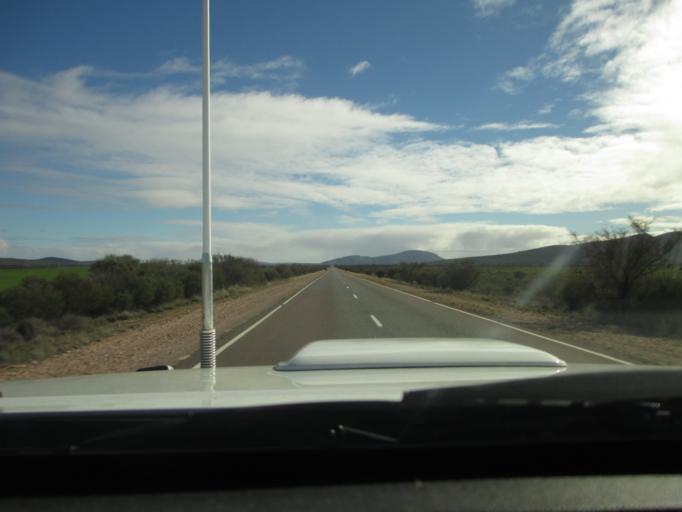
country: AU
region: South Australia
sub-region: Flinders Ranges
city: Quorn
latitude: -31.8678
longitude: 138.4068
